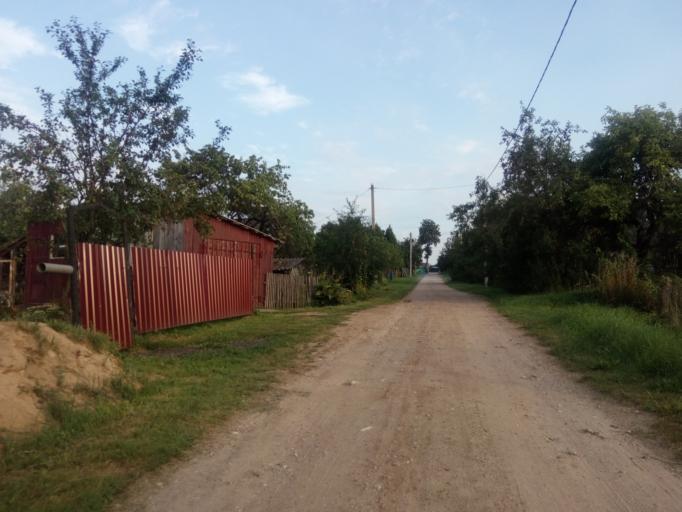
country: BY
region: Vitebsk
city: Dzisna
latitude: 55.6757
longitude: 28.3264
